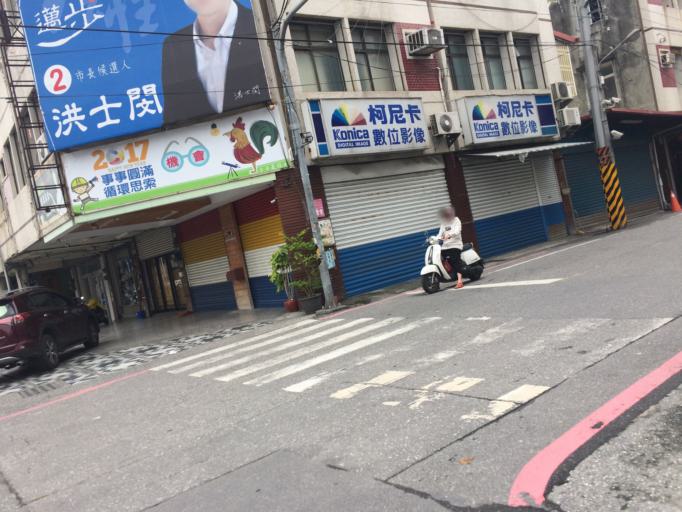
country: TW
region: Taiwan
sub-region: Hualien
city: Hualian
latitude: 23.9723
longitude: 121.5999
